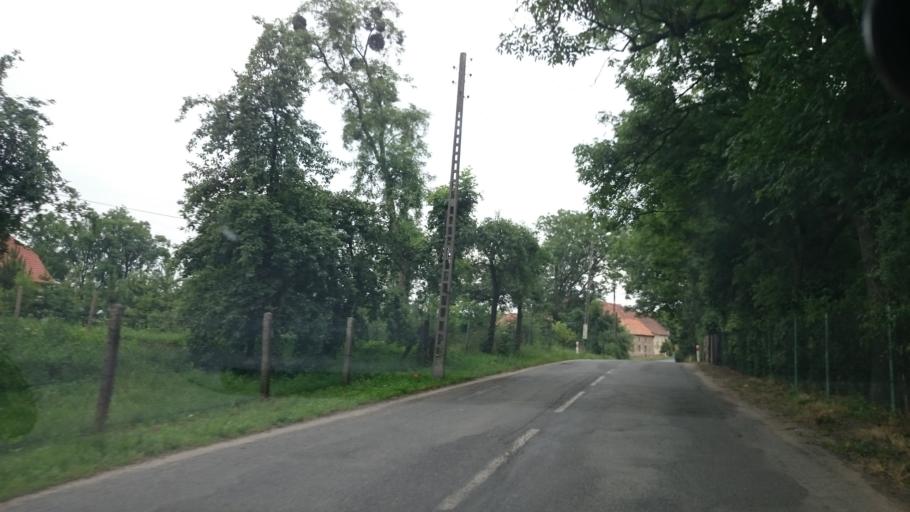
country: PL
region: Lower Silesian Voivodeship
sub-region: Powiat strzelinski
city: Przeworno
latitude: 50.6431
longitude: 17.2264
